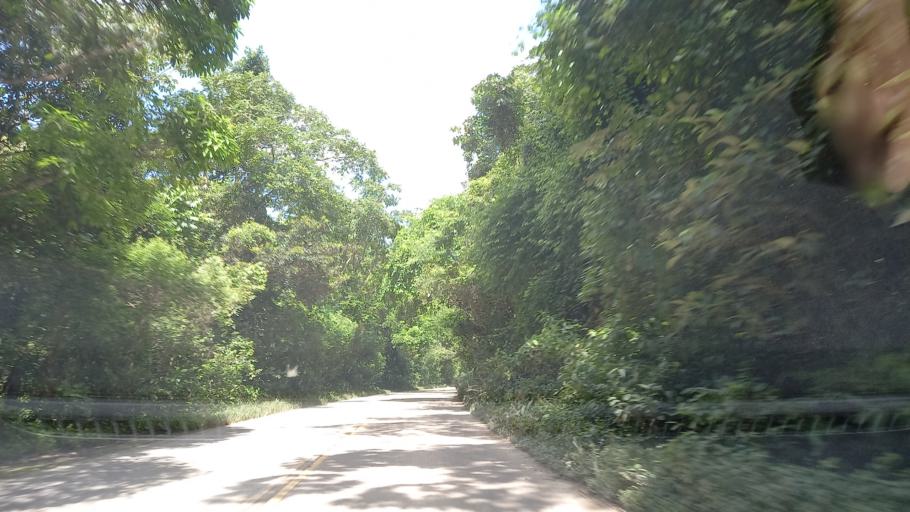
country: BR
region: Pernambuco
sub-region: Rio Formoso
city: Rio Formoso
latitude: -8.7229
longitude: -35.1736
